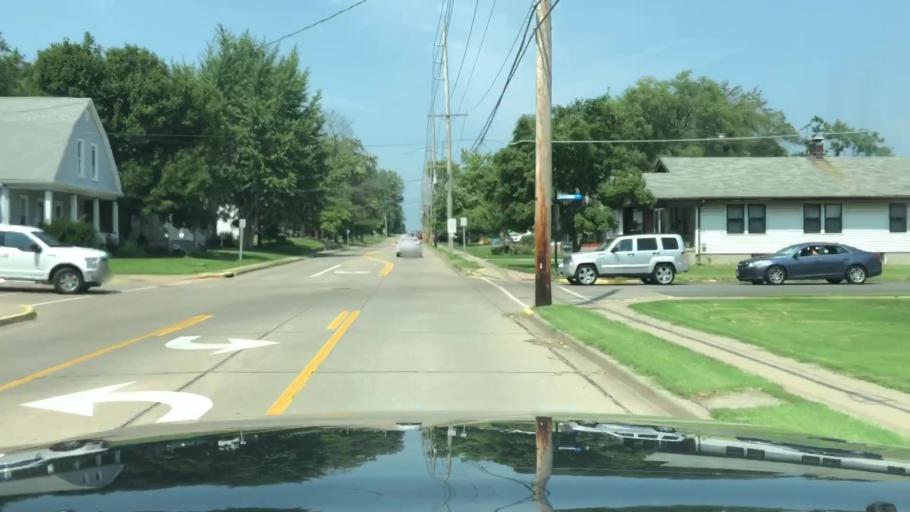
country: US
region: Missouri
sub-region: Saint Charles County
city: Saint Charles
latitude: 38.7887
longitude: -90.4943
